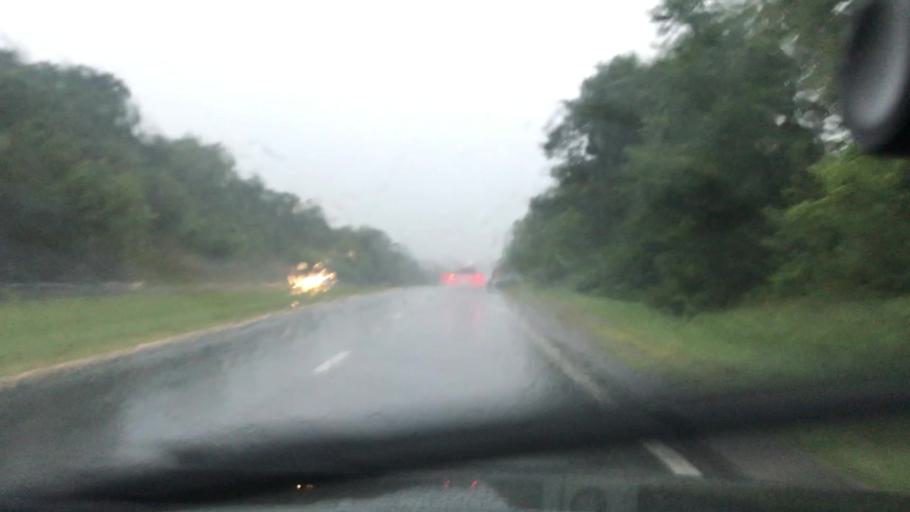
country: US
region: Virginia
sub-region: Giles County
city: Pearisburg
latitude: 37.3368
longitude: -80.7072
